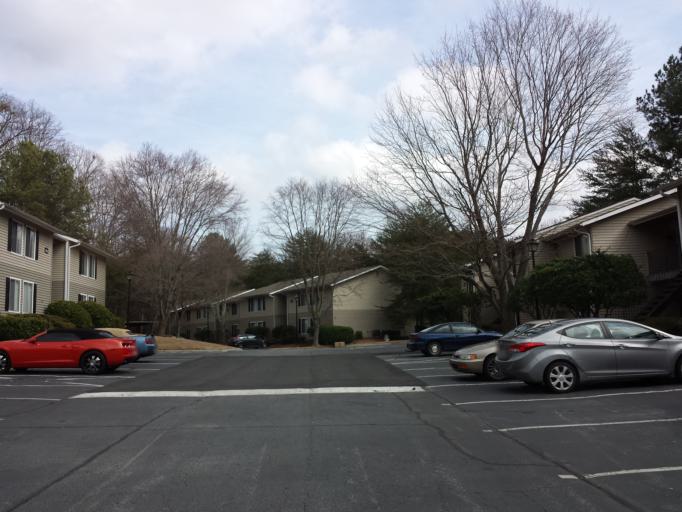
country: US
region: Georgia
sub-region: Cobb County
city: Vinings
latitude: 33.9079
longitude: -84.4702
